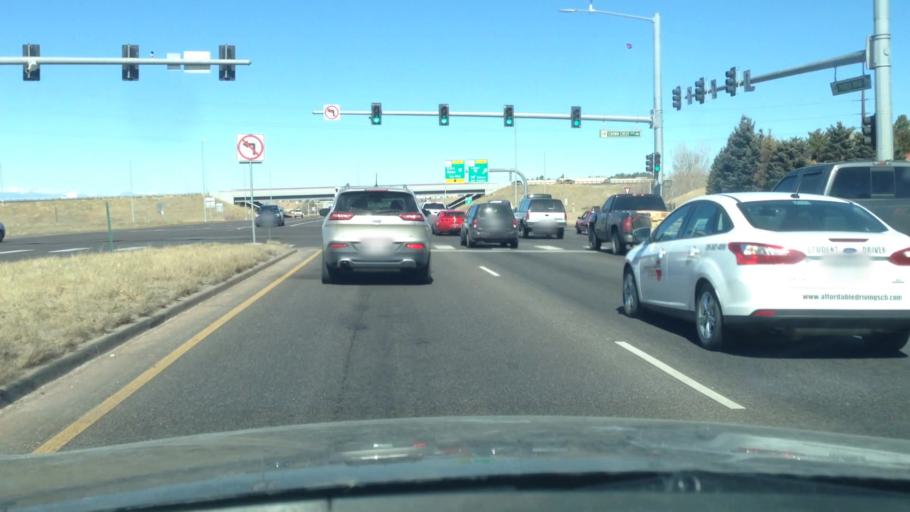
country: US
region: Colorado
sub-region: Douglas County
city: Parker
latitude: 39.5493
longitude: -104.7746
